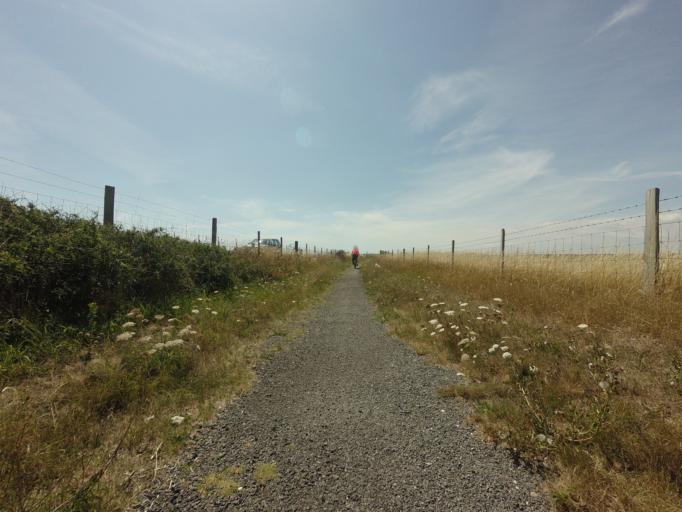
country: GB
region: England
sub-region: Kent
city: Lydd
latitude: 50.9302
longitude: 0.8363
